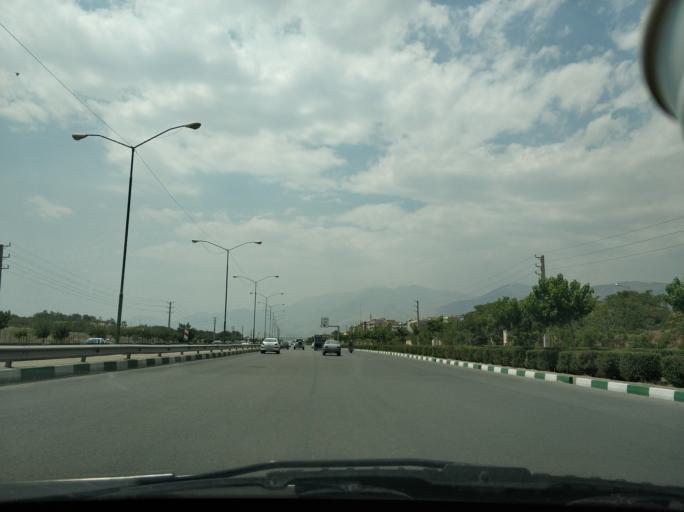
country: IR
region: Tehran
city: Tajrish
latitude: 35.7640
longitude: 51.5673
